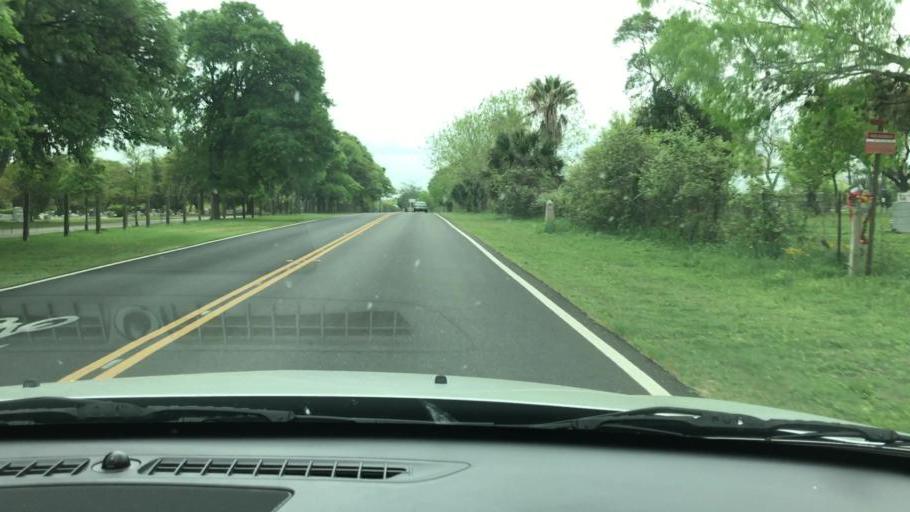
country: US
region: Texas
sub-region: Bexar County
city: San Antonio
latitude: 29.3457
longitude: -98.4718
